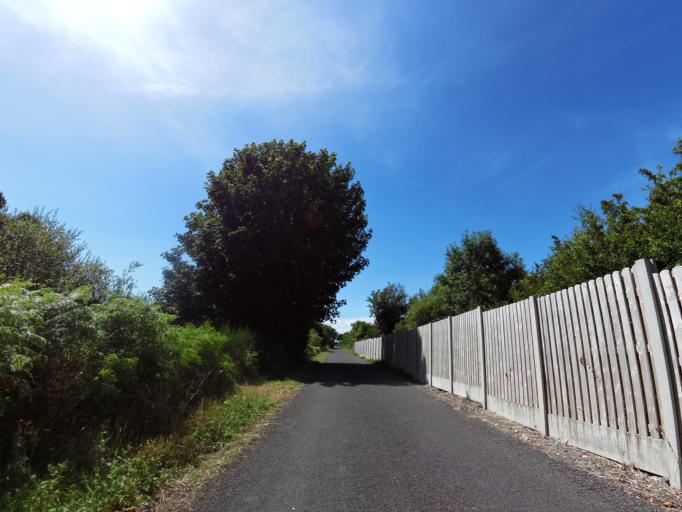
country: IE
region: Munster
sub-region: Waterford
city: Portlaw
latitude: 52.2266
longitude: -7.3235
